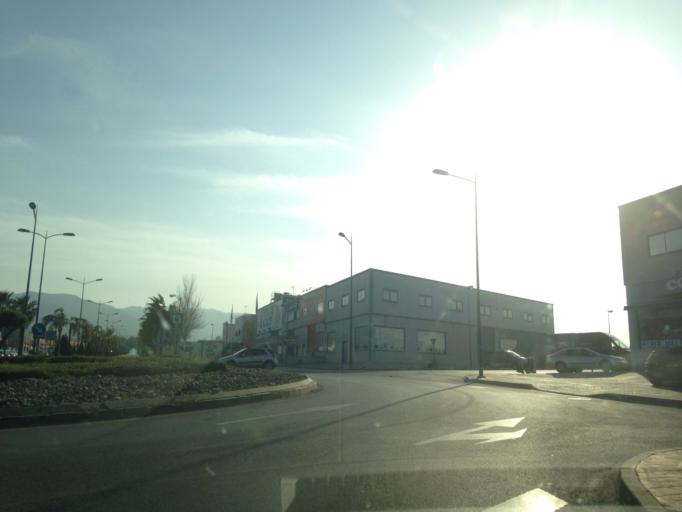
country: ES
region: Andalusia
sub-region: Provincia de Malaga
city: Alhaurin de la Torre
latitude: 36.6746
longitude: -4.5491
